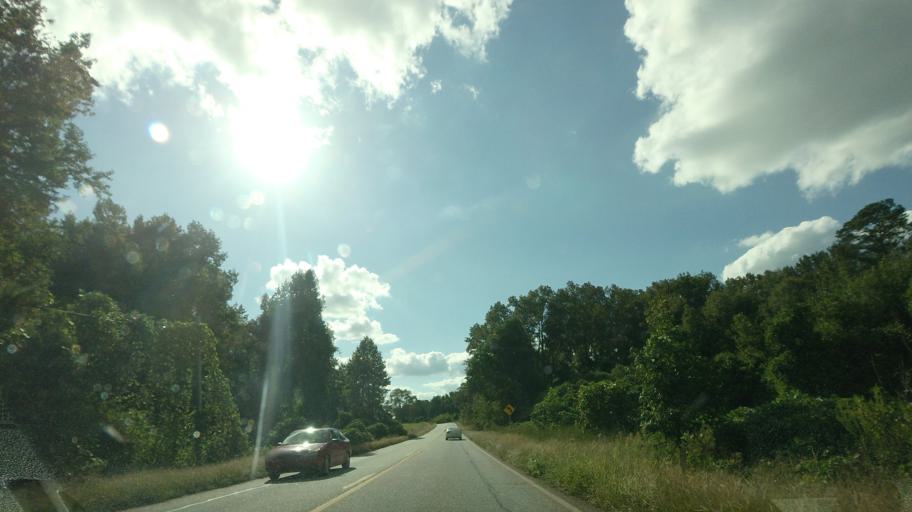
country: US
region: Georgia
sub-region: Lamar County
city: Barnesville
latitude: 33.0543
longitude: -84.1021
